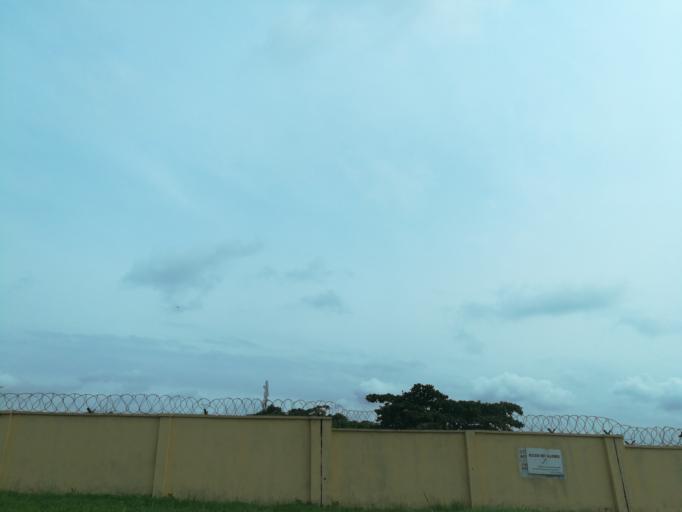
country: NG
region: Lagos
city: Oshodi
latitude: 6.5659
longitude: 3.3241
